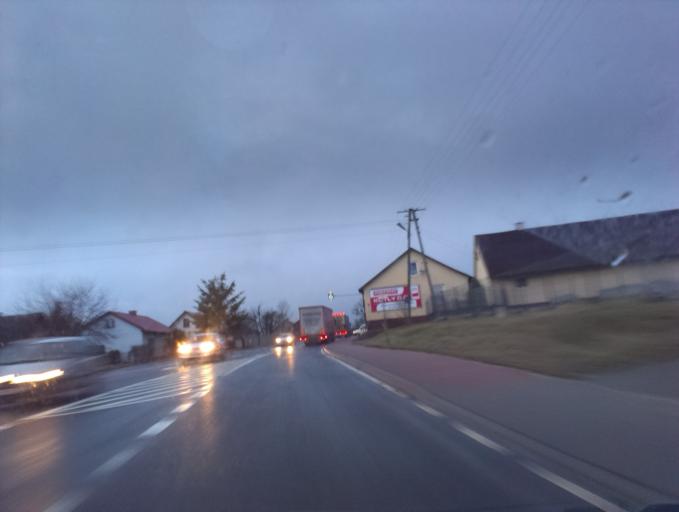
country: PL
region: Lodz Voivodeship
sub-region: Powiat opoczynski
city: Zarnow
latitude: 51.2110
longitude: 20.1962
